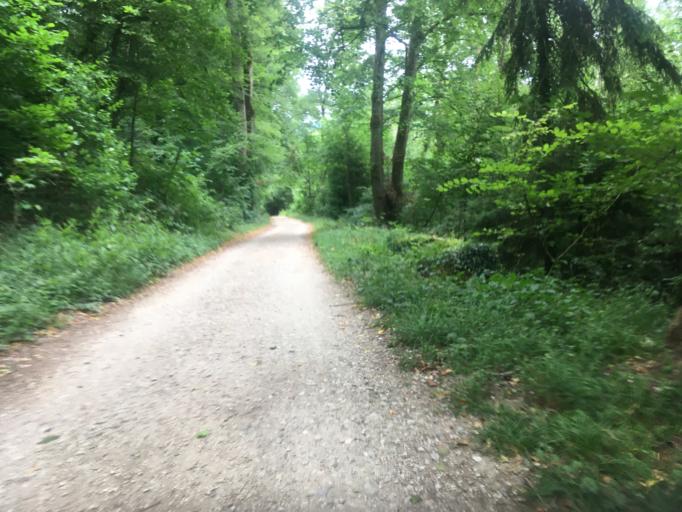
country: CH
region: Bern
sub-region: Jura bernois
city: La Neuveville
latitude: 47.0733
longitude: 7.1472
